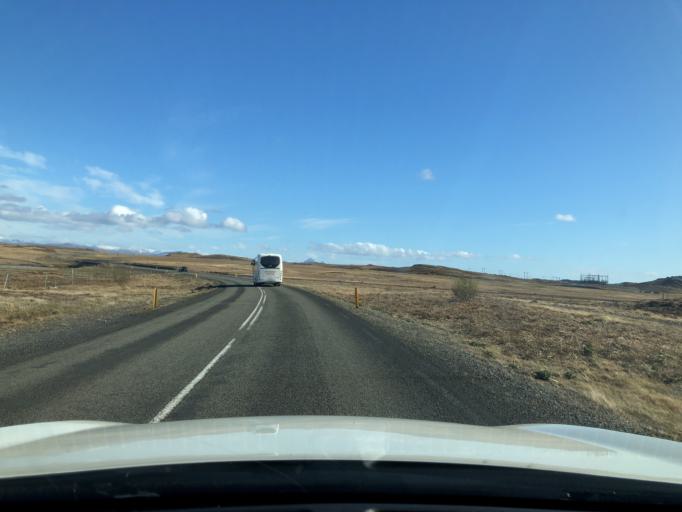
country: IS
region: West
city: Borgarnes
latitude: 64.5495
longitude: -21.7322
